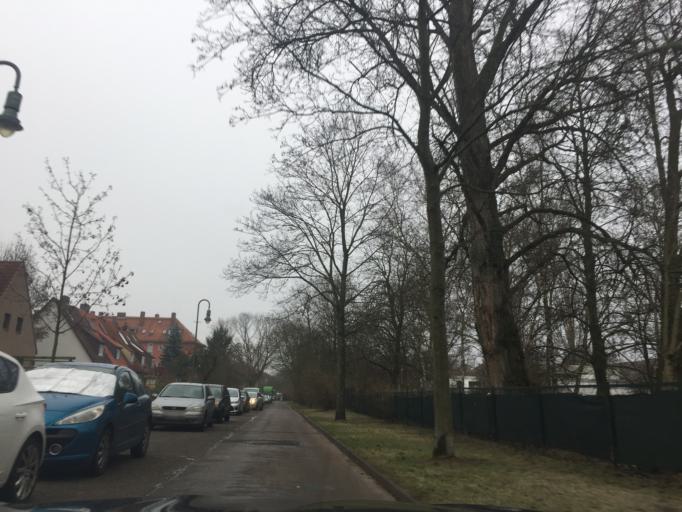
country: DE
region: Berlin
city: Tegel
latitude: 52.5864
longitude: 13.3037
